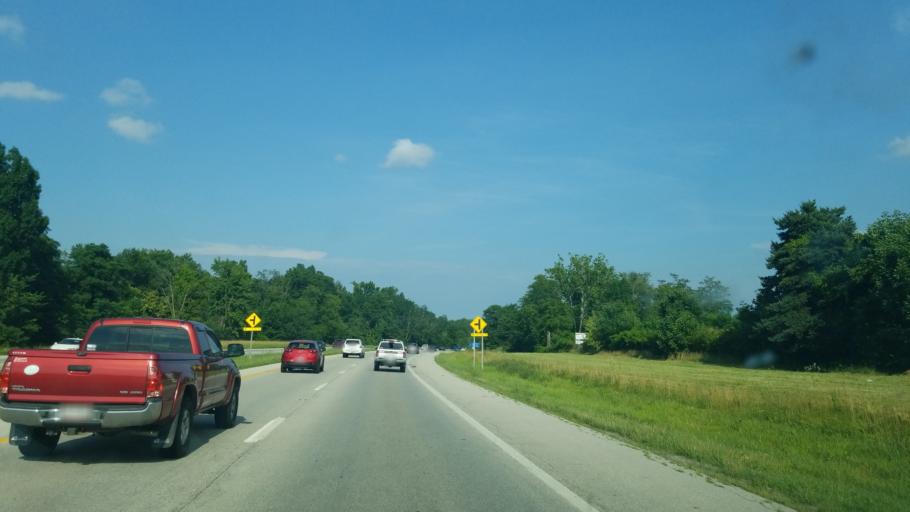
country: US
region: Ohio
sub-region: Clermont County
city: Batavia
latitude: 39.0883
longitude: -84.2093
